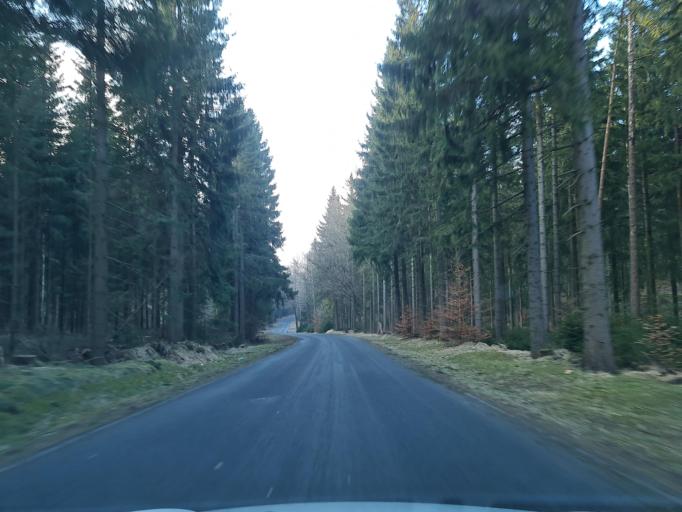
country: DE
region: Saxony
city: Muldenhammer
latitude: 50.4943
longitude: 12.4549
